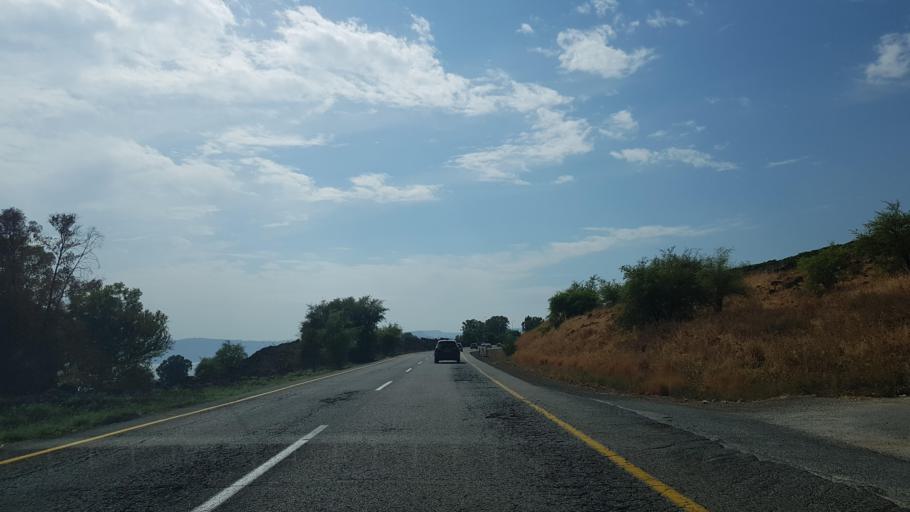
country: SY
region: Quneitra
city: Al Butayhah
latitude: 32.8957
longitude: 35.6028
